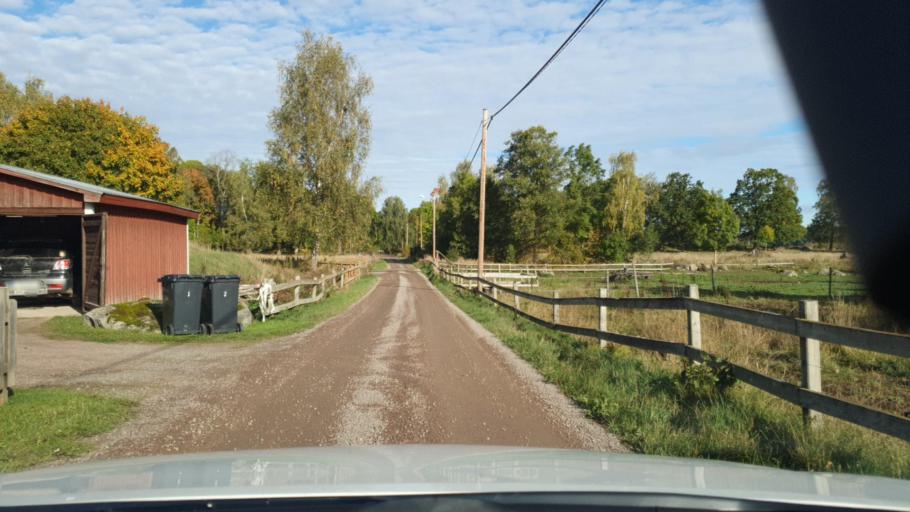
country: SE
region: Kalmar
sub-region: Hultsfreds Kommun
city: Malilla
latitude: 57.3227
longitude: 15.8100
